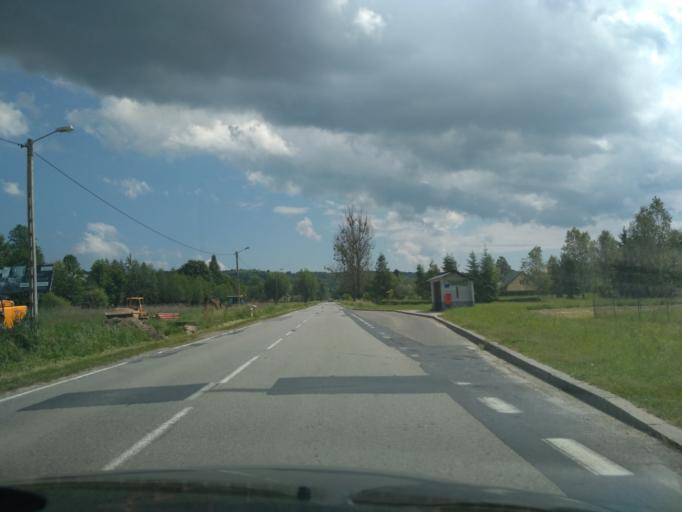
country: PL
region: Subcarpathian Voivodeship
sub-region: Powiat rzeszowski
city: Hyzne
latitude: 49.9274
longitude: 22.1411
